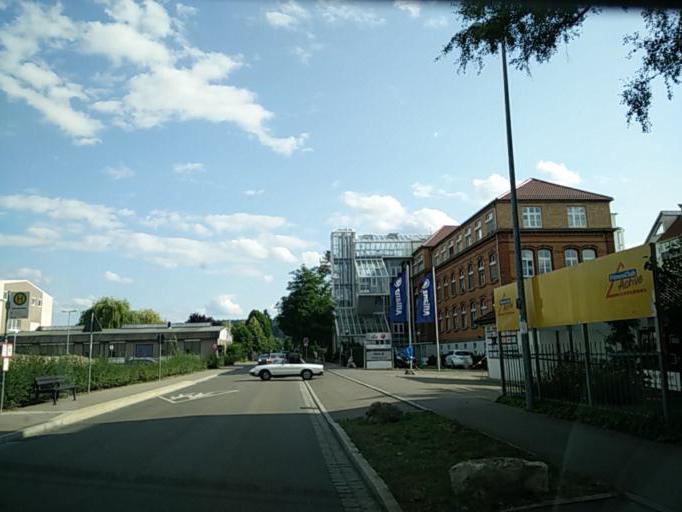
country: DE
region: Baden-Wuerttemberg
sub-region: Tuebingen Region
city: Tuebingen
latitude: 48.5116
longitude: 9.0518
